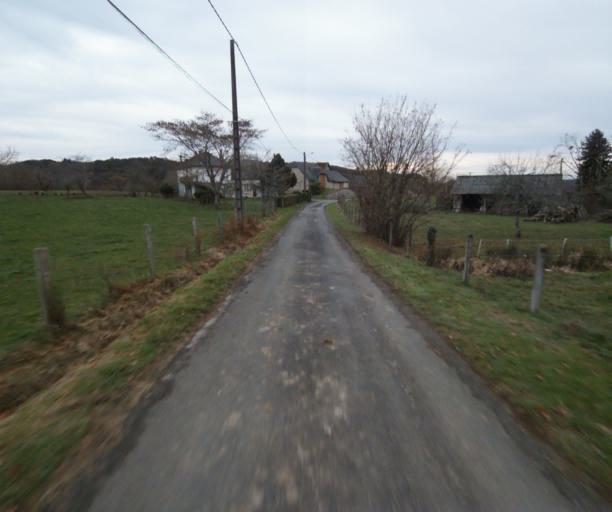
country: FR
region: Limousin
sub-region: Departement de la Correze
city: Saint-Mexant
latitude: 45.2501
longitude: 1.6582
